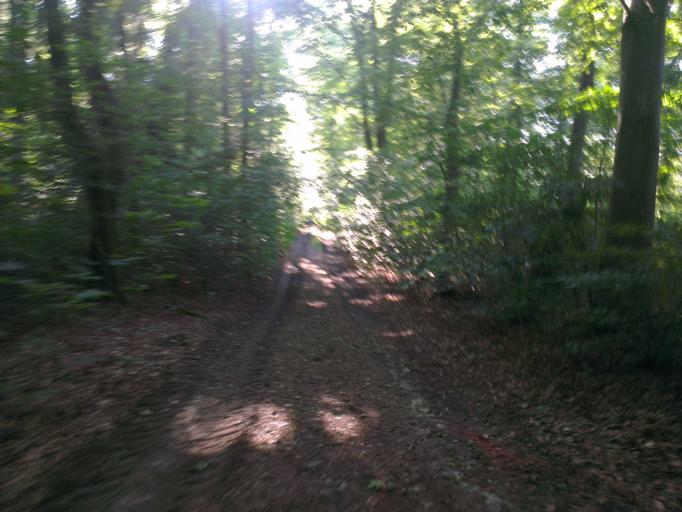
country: DK
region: Capital Region
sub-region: Frederikssund Kommune
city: Skibby
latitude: 55.7907
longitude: 11.9557
